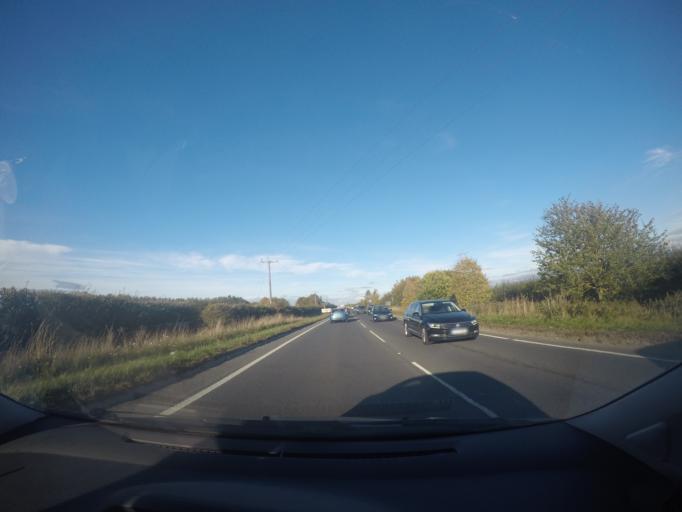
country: GB
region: England
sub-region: City of York
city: Nether Poppleton
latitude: 53.9640
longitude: -1.1497
